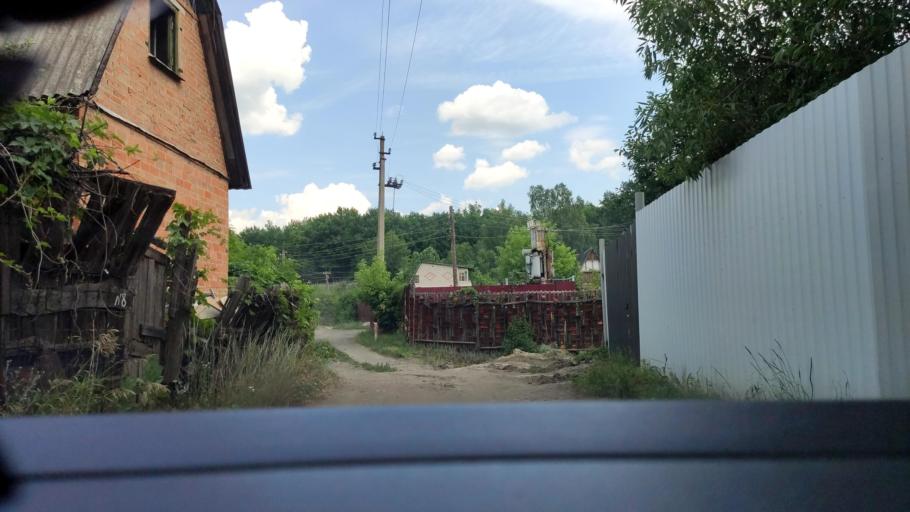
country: RU
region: Voronezj
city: Maslovka
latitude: 51.6080
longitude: 39.2868
